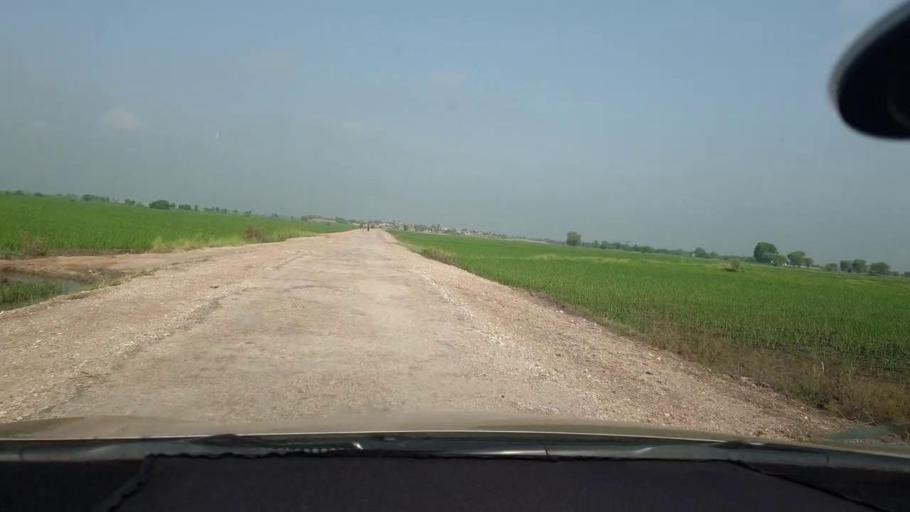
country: PK
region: Sindh
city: Kambar
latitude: 27.5380
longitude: 68.0562
